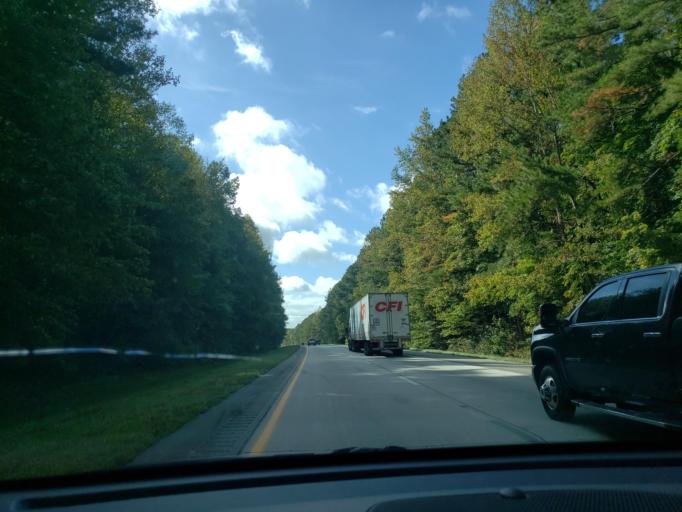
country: US
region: North Carolina
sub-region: Granville County
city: Oxford
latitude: 36.3224
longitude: -78.5152
